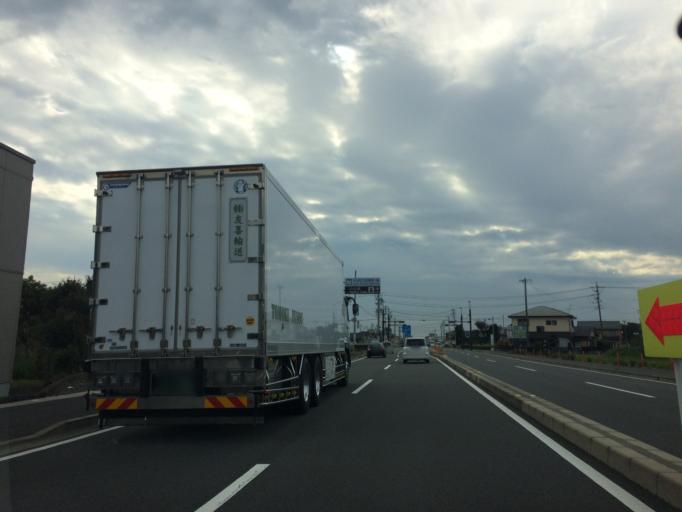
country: JP
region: Shizuoka
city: Shimada
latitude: 34.7810
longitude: 138.2516
